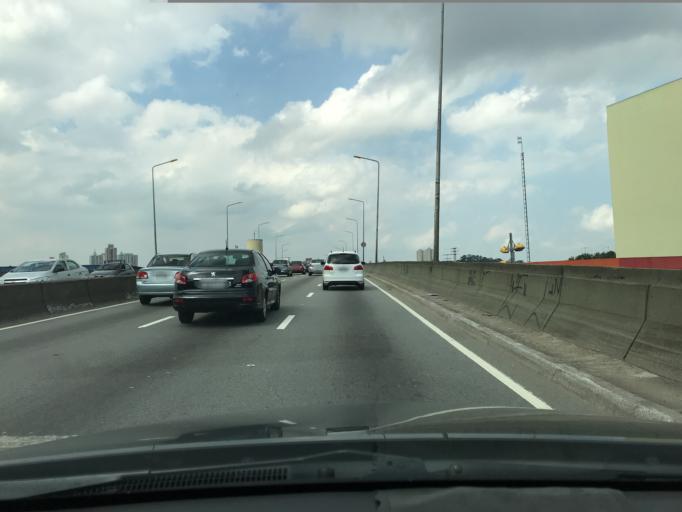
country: BR
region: Sao Paulo
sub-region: Santo Andre
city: Santo Andre
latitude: -23.6538
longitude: -46.5295
